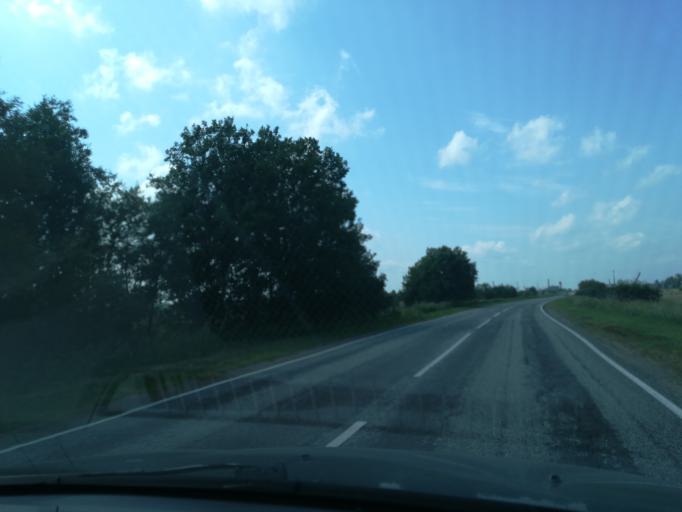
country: RU
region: Leningrad
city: Kopor'ye
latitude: 59.7080
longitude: 29.0835
